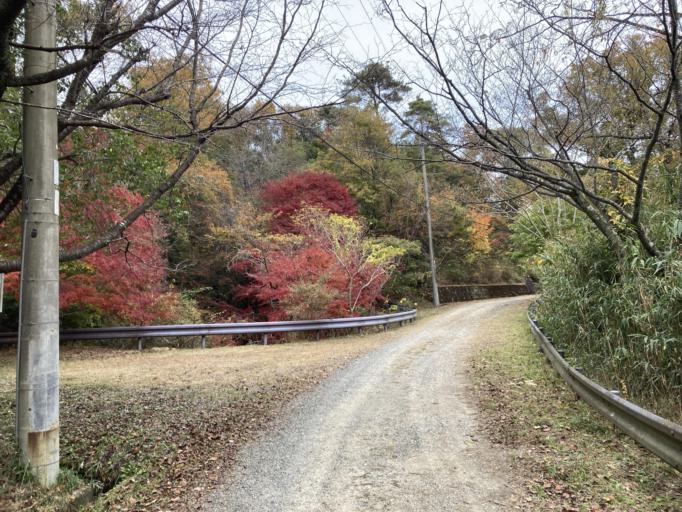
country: JP
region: Osaka
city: Hirakata
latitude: 34.7658
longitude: 135.7053
